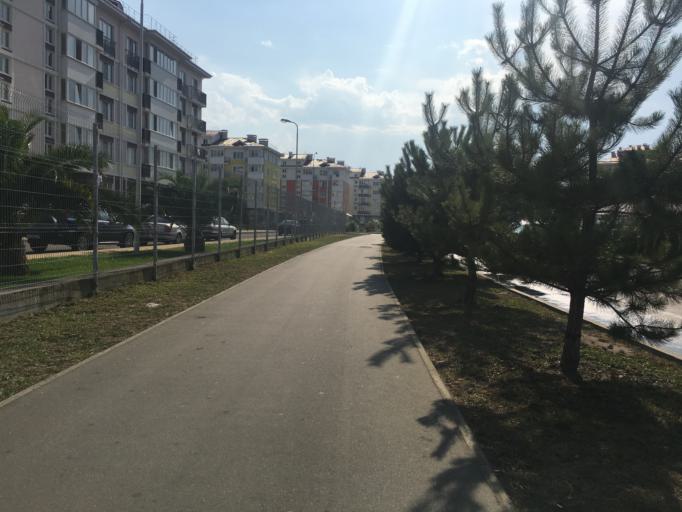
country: RU
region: Krasnodarskiy
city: Vysokoye
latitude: 43.3919
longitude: 39.9939
